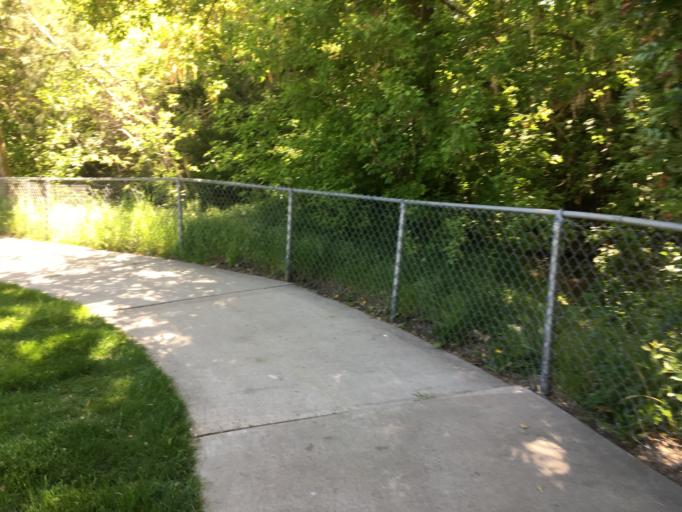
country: US
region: Utah
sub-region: Davis County
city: Layton
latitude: 41.0670
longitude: -111.9633
